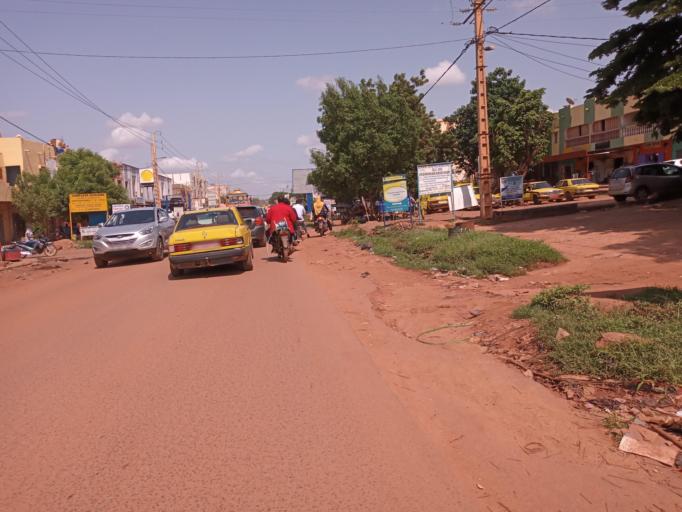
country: ML
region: Bamako
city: Bamako
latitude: 12.5974
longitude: -8.0238
